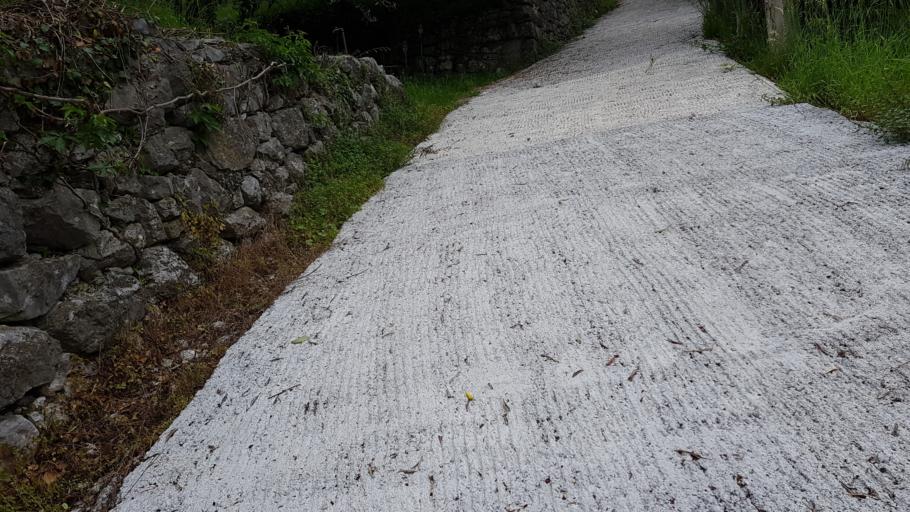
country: IT
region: Trentino-Alto Adige
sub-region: Provincia di Trento
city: Padergnone
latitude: 46.0703
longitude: 10.9816
